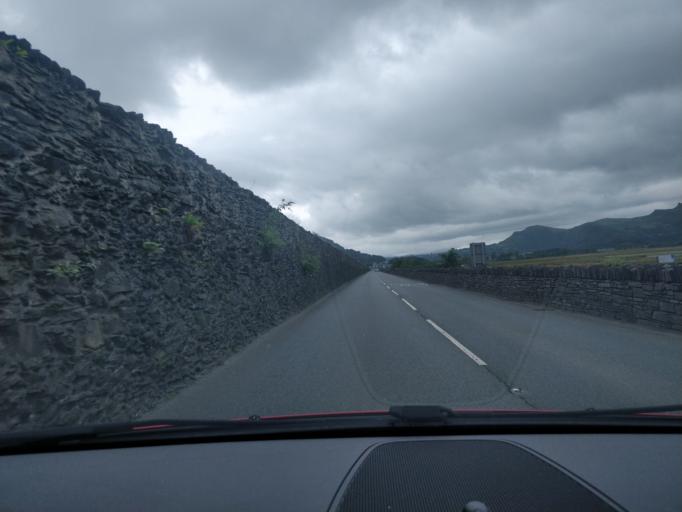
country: GB
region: Wales
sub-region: Gwynedd
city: Porthmadog
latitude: 52.9198
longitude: -4.1088
